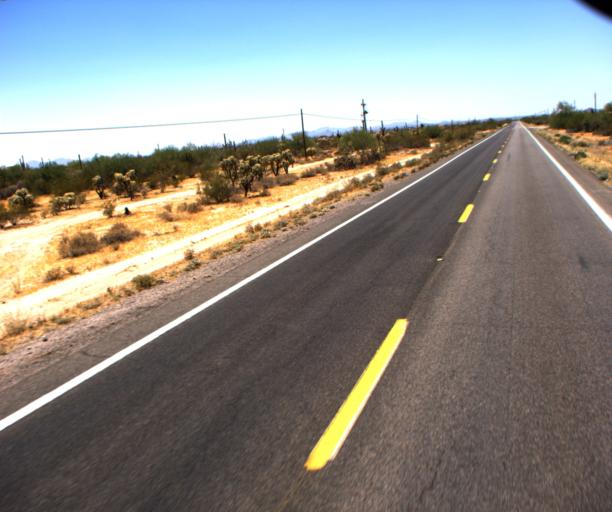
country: US
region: Arizona
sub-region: Pinal County
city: Florence
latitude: 32.9655
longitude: -111.3402
